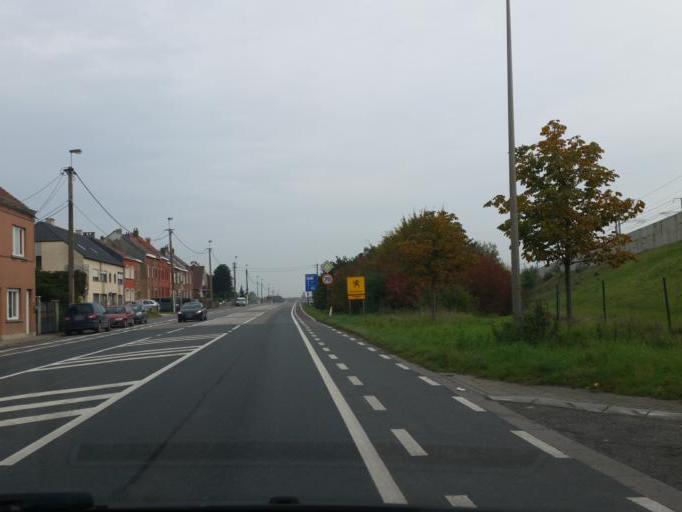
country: BE
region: Wallonia
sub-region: Province du Brabant Wallon
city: Tubize
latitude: 50.7068
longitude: 4.2116
